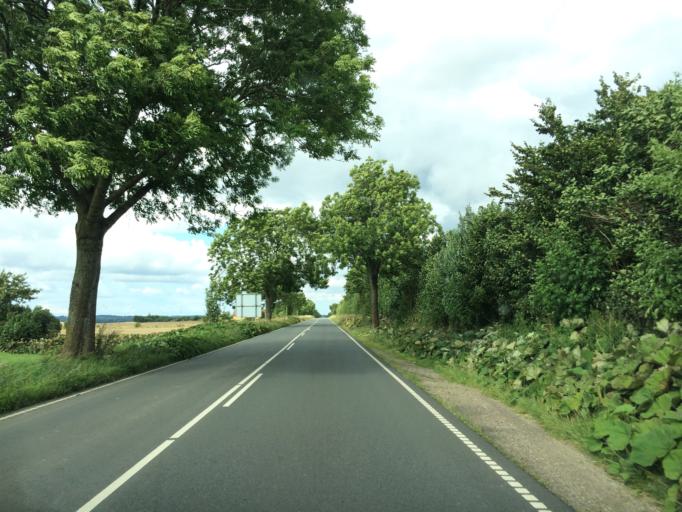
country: DK
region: South Denmark
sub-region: Assens Kommune
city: Harby
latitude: 55.2060
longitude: 10.1575
